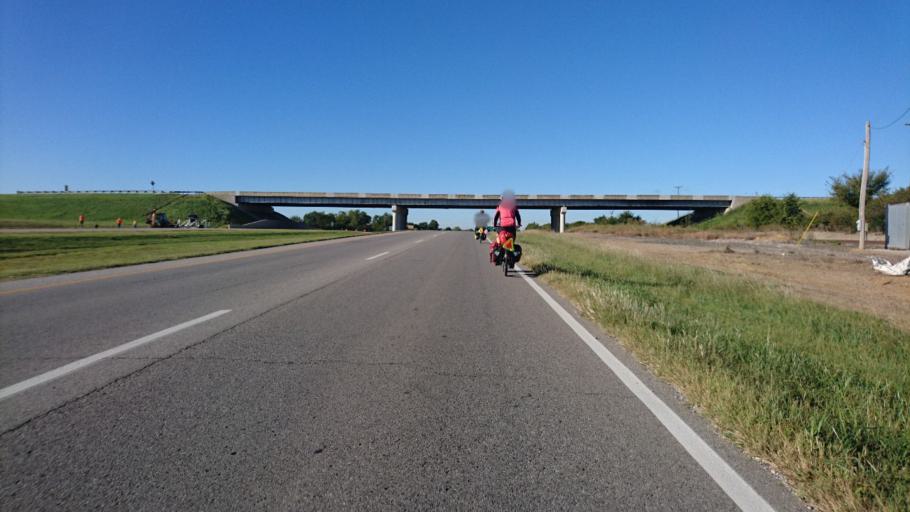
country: US
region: Oklahoma
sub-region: Rogers County
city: Verdigris
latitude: 36.2470
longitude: -95.6717
